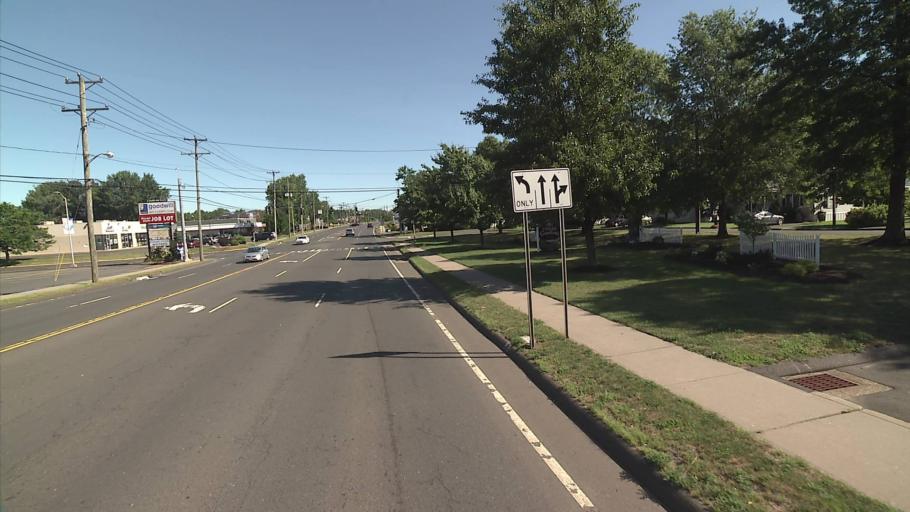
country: US
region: Connecticut
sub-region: Hartford County
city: Plainville
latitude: 41.6255
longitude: -72.8733
